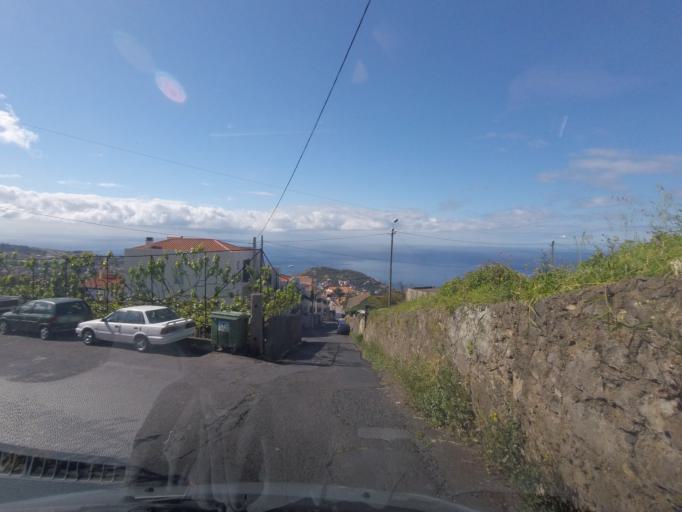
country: PT
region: Madeira
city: Camara de Lobos
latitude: 32.6660
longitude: -16.9755
